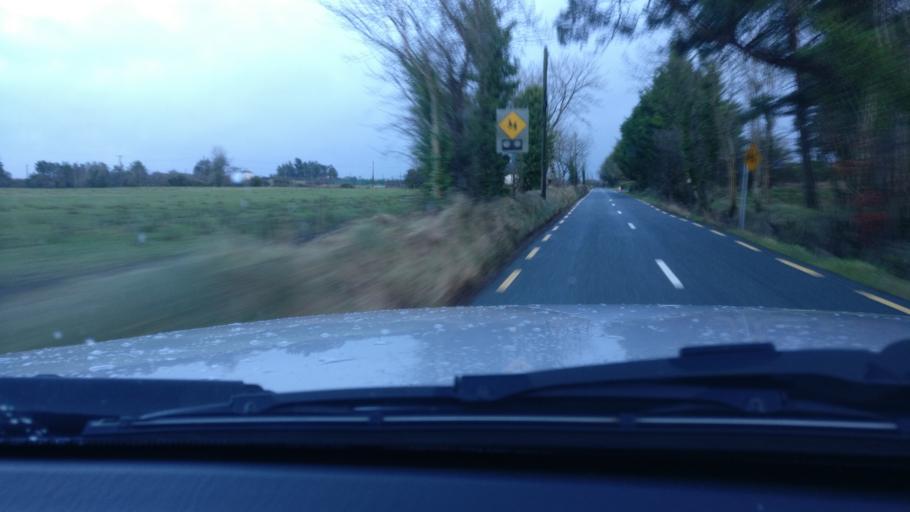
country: IE
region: Connaught
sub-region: County Galway
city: Loughrea
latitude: 53.2235
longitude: -8.3841
